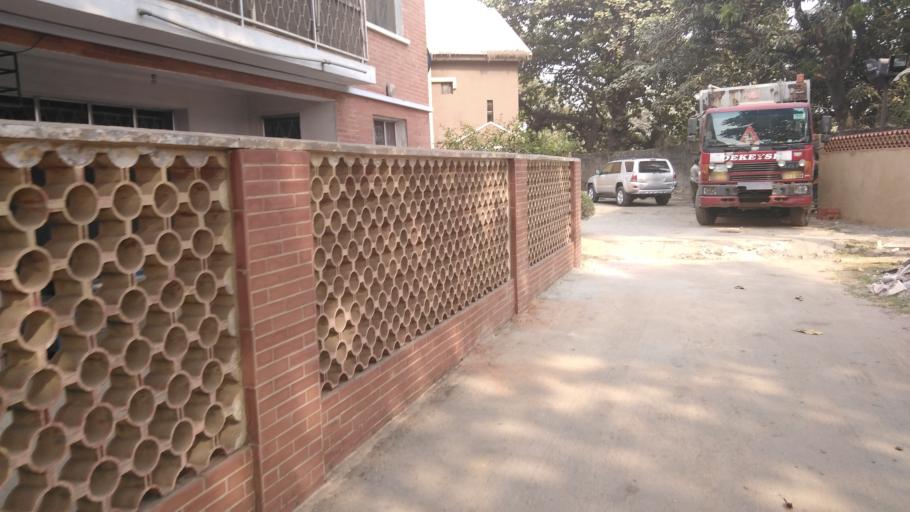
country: NG
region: Lagos
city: Apapa
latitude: 6.4490
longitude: 3.3673
